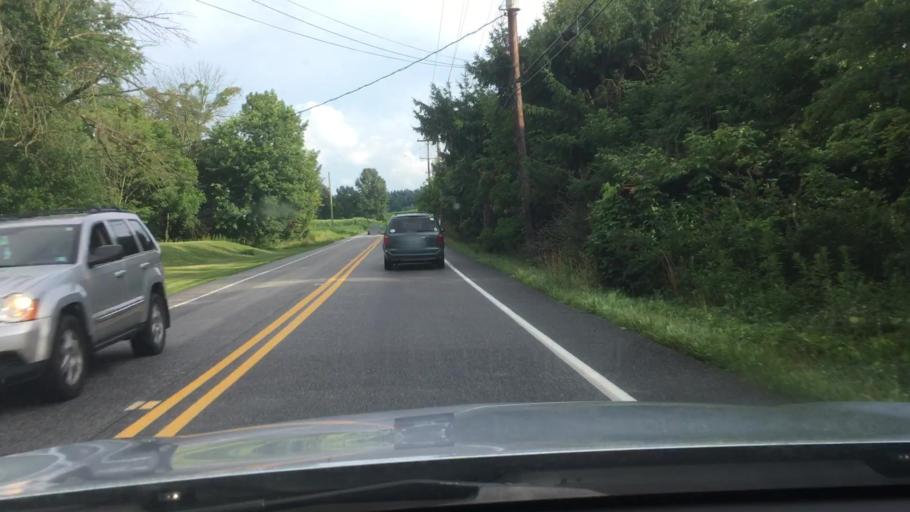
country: US
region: Pennsylvania
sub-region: York County
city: Dillsburg
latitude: 40.1308
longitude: -77.0385
